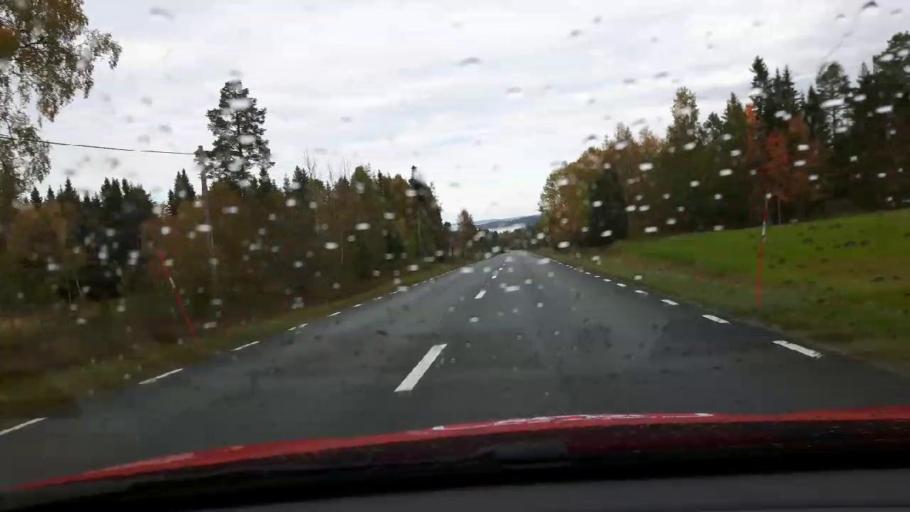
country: SE
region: Jaemtland
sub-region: Krokoms Kommun
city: Krokom
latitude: 63.1173
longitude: 14.2933
